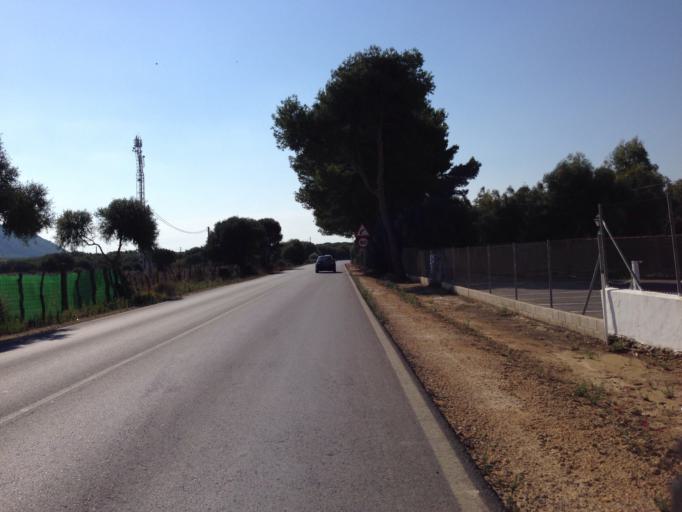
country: ES
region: Andalusia
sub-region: Provincia de Cadiz
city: Vejer de la Frontera
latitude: 36.2065
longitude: -6.0349
